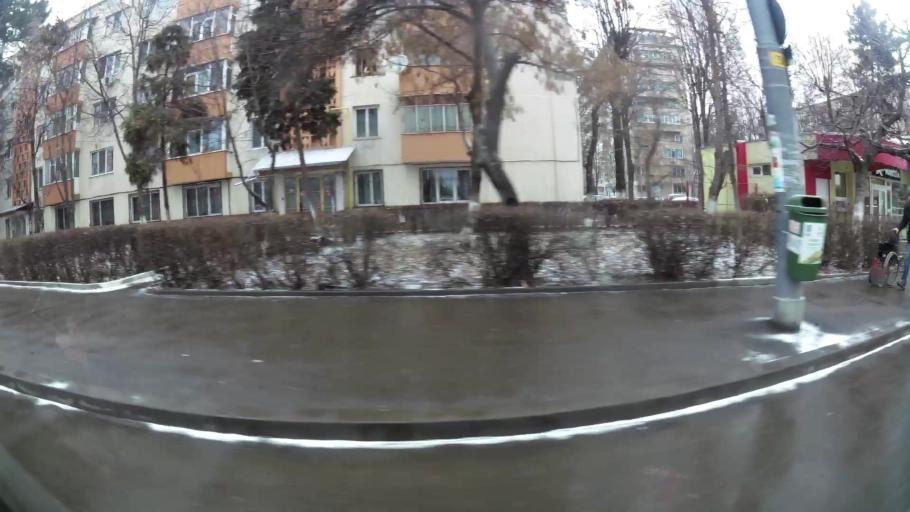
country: RO
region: Prahova
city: Ploiesti
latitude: 44.9557
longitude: 26.0040
